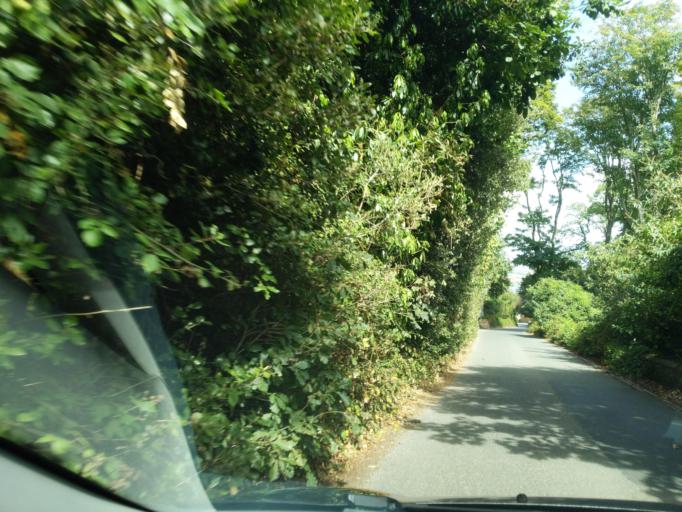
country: GB
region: England
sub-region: Devon
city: Salcombe
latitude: 50.2325
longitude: -3.7750
